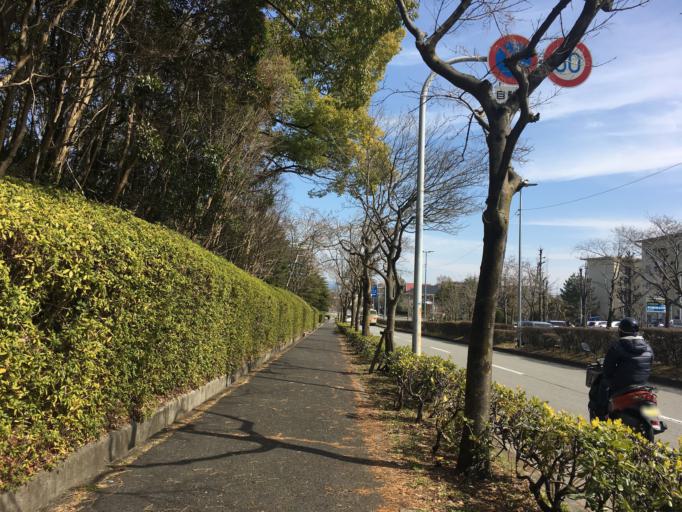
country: JP
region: Osaka
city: Mino
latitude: 34.8160
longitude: 135.5022
